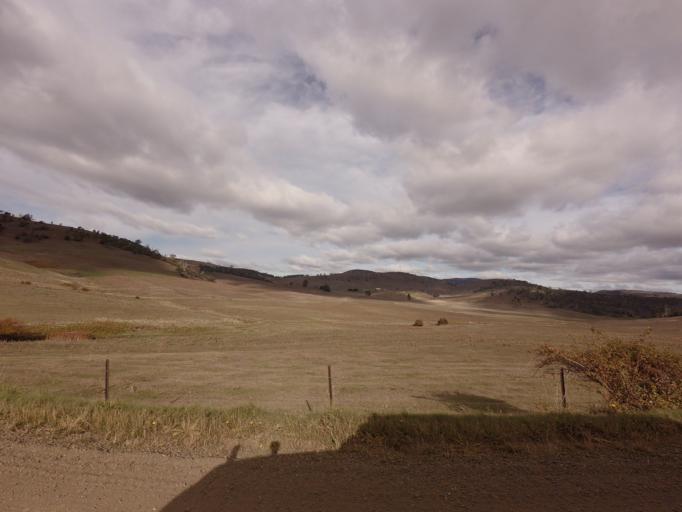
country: AU
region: Tasmania
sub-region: Brighton
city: Bridgewater
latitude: -42.4608
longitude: 147.2758
